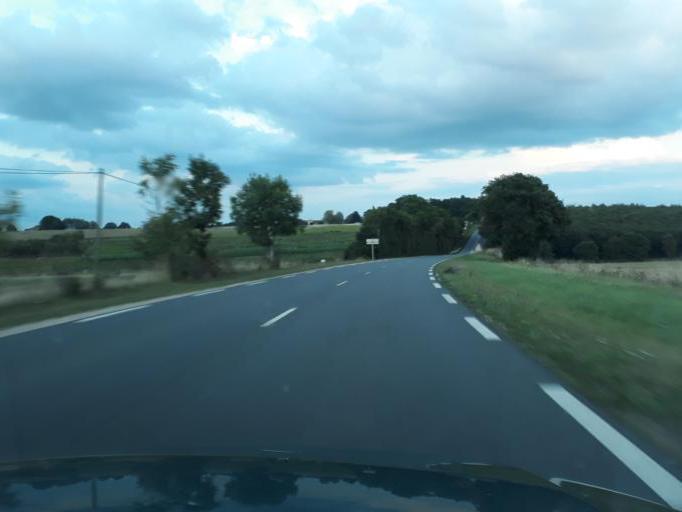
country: FR
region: Centre
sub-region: Departement du Loir-et-Cher
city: Aze
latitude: 47.8996
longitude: 0.9381
